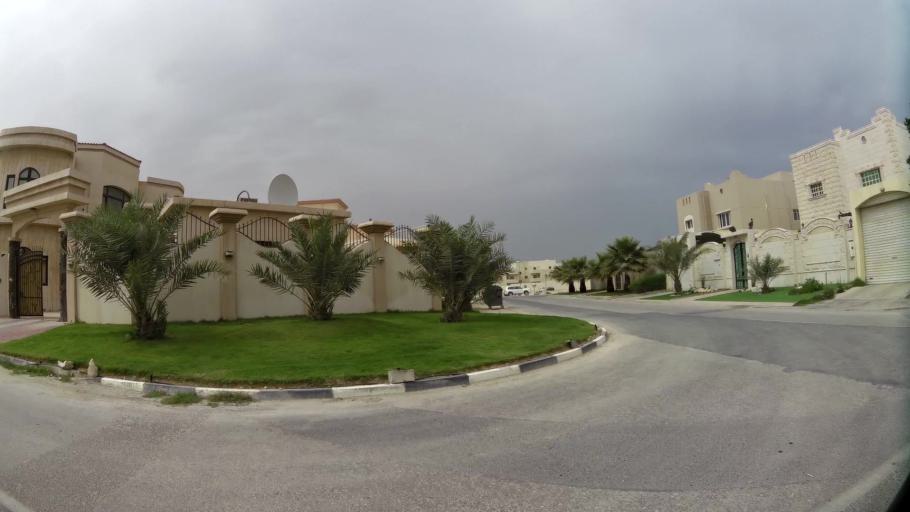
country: QA
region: Baladiyat ar Rayyan
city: Ar Rayyan
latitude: 25.3418
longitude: 51.4734
